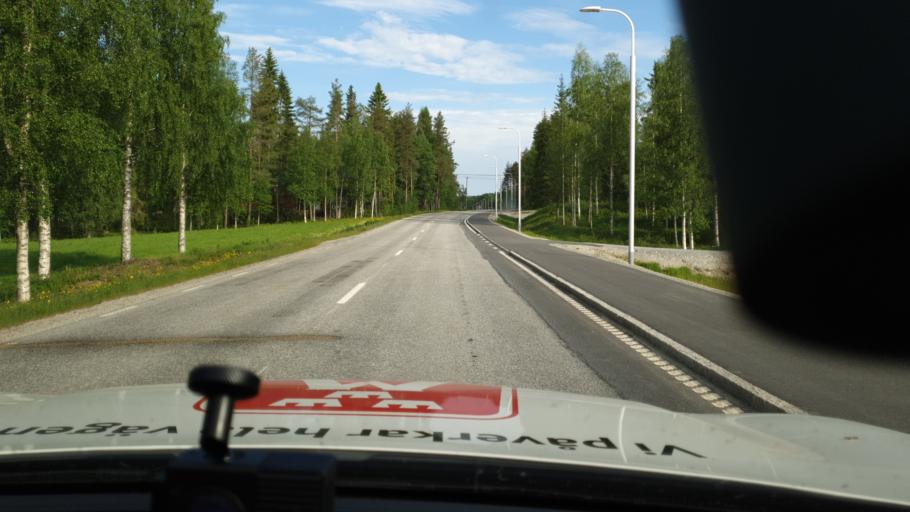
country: SE
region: Vaesterbotten
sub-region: Bjurholms Kommun
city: Bjurholm
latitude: 64.2299
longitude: 19.3544
